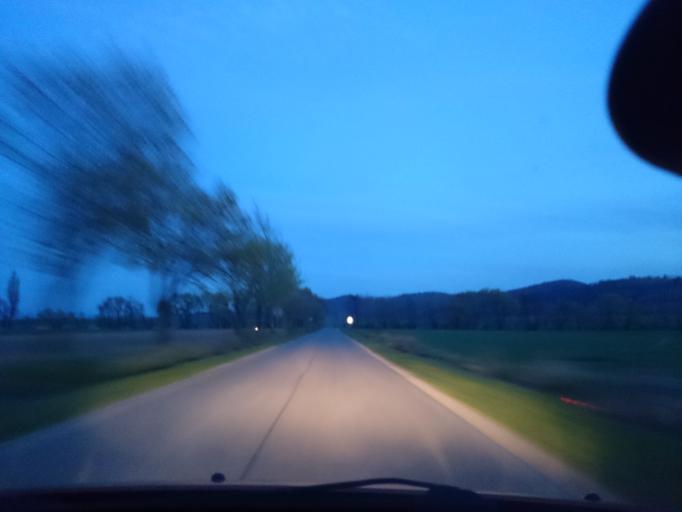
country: PL
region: Lower Silesian Voivodeship
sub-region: Powiat zabkowicki
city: Budzow
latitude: 50.5703
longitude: 16.6831
